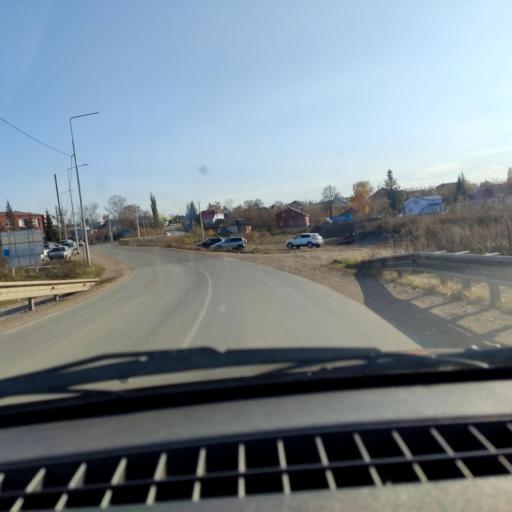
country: RU
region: Bashkortostan
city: Avdon
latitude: 54.5014
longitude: 55.8808
